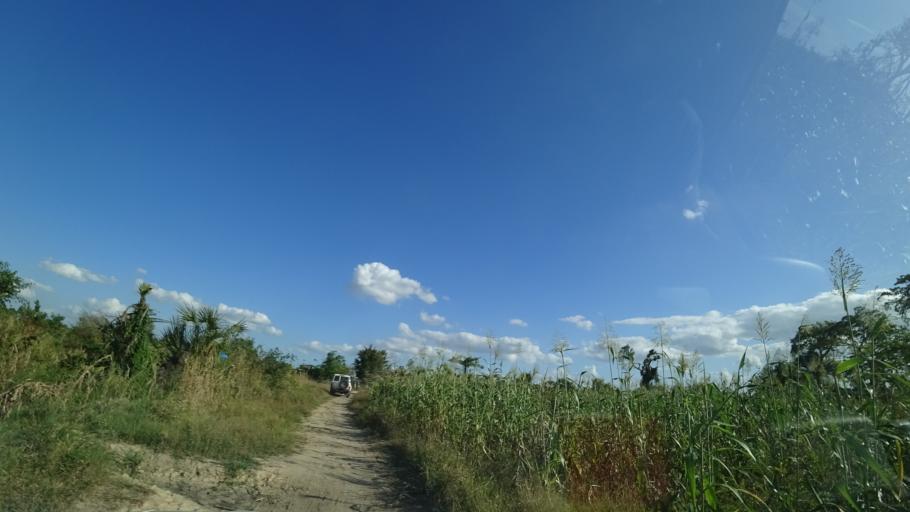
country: MZ
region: Sofala
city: Dondo
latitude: -19.3527
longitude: 34.5879
